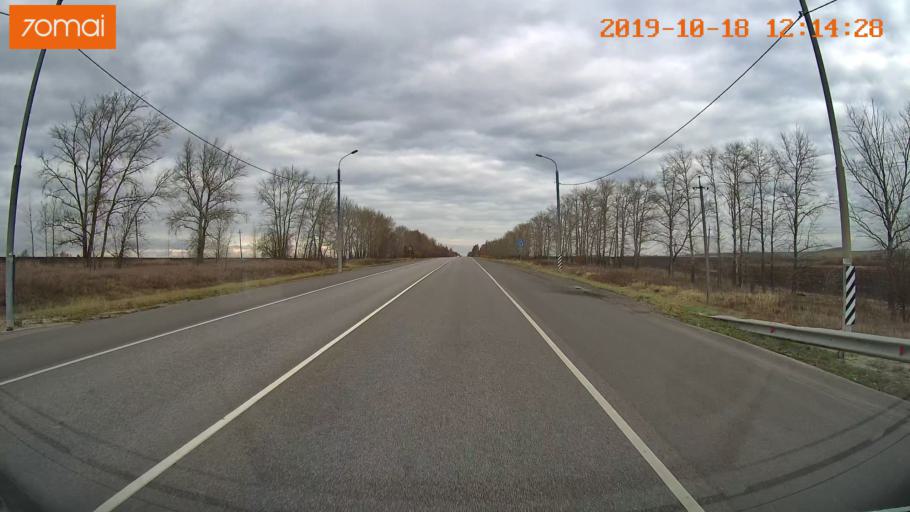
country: RU
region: Rjazan
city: Zakharovo
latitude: 54.4310
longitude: 39.3836
